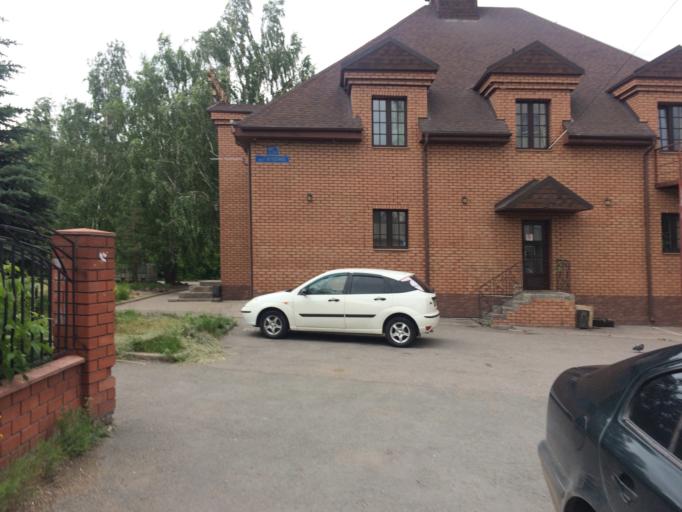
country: RU
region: Chelyabinsk
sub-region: Gorod Magnitogorsk
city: Magnitogorsk
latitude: 53.4109
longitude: 58.9802
